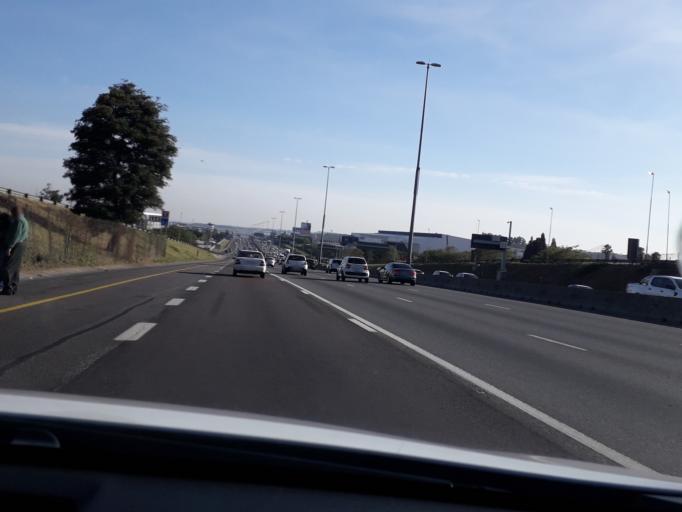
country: ZA
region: Gauteng
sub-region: City of Johannesburg Metropolitan Municipality
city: Midrand
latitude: -25.9790
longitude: 28.1265
